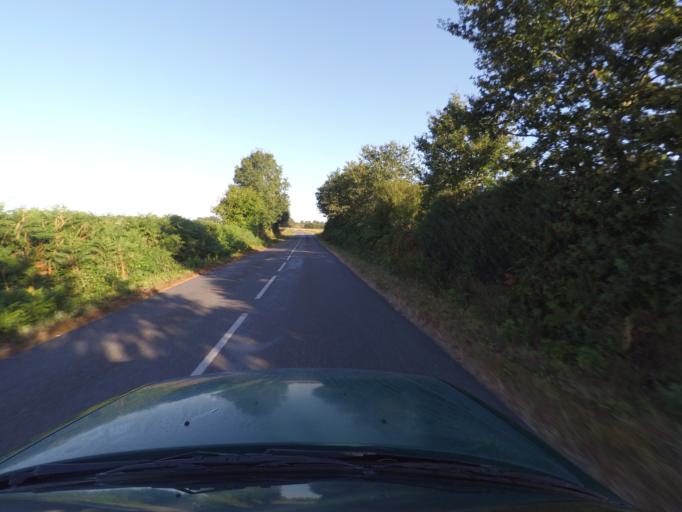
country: FR
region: Pays de la Loire
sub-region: Departement de la Loire-Atlantique
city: Montbert
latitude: 47.0419
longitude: -1.4737
